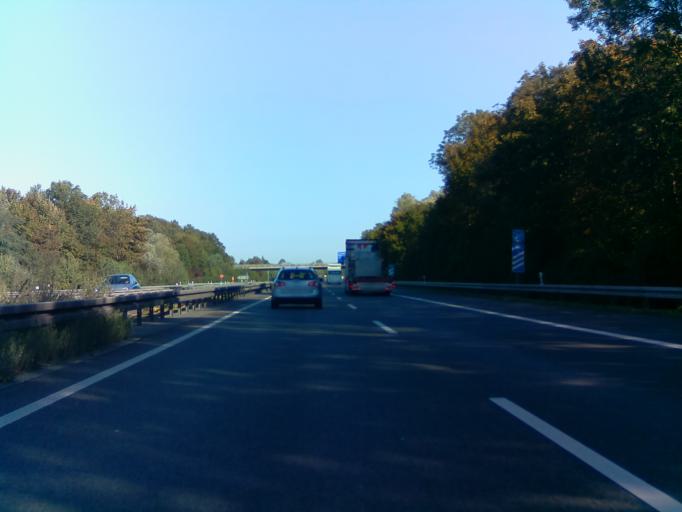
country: DE
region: Hesse
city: Zwingenberg
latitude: 49.7187
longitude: 8.5950
